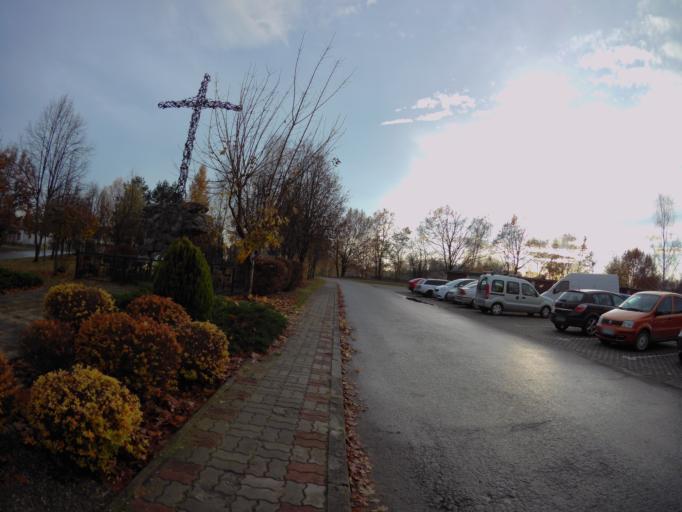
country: PL
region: Subcarpathian Voivodeship
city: Nowa Sarzyna
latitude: 50.3164
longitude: 22.3393
